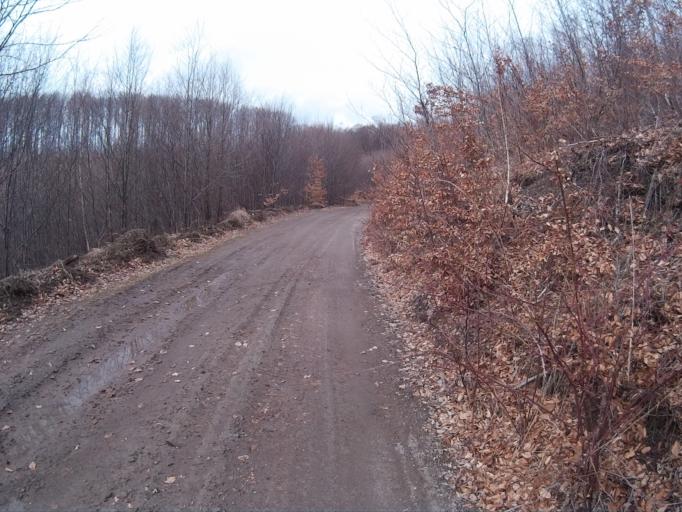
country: HU
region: Borsod-Abauj-Zemplen
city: Tolcsva
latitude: 48.4033
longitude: 21.4232
